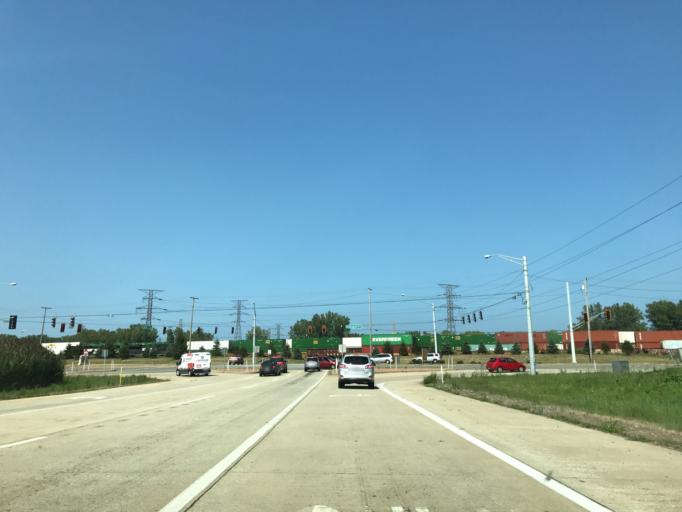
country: US
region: Indiana
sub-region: Lake County
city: Whiting
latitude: 41.6978
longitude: -87.5206
